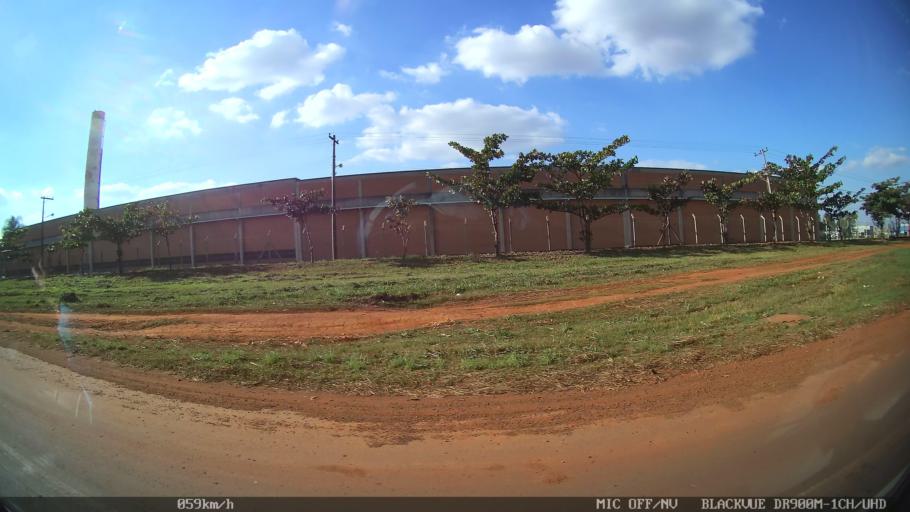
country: BR
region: Sao Paulo
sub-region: Santa Barbara D'Oeste
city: Santa Barbara d'Oeste
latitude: -22.7781
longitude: -47.3745
